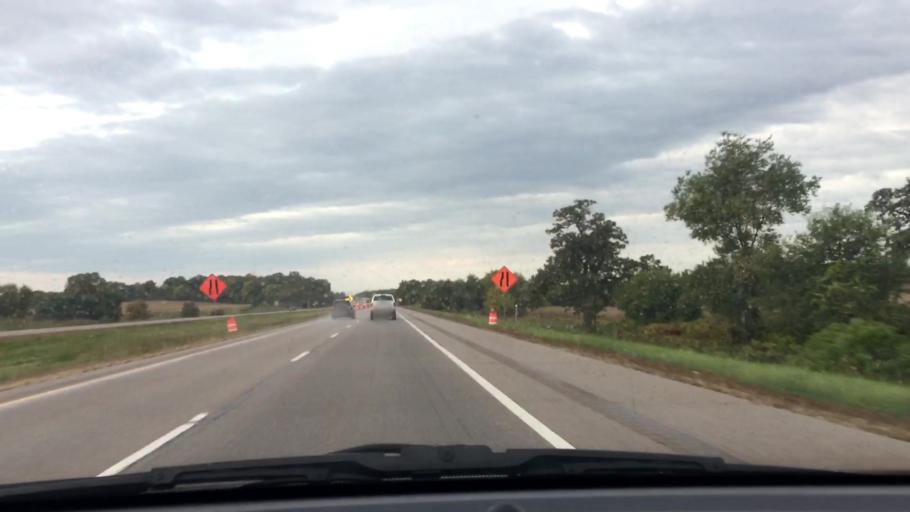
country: US
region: Wisconsin
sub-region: Rock County
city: Clinton
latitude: 42.5497
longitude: -88.9327
